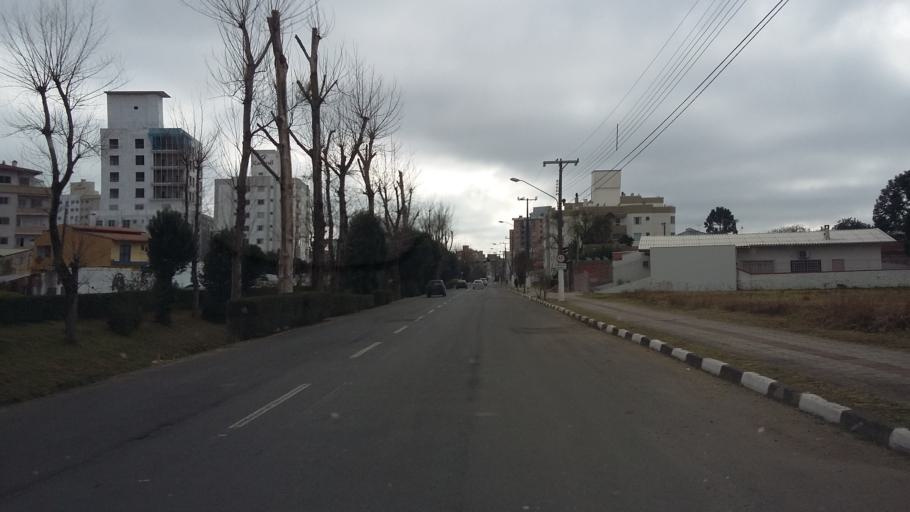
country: BR
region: Santa Catarina
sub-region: Lages
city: Lages
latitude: -27.8219
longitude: -50.3220
